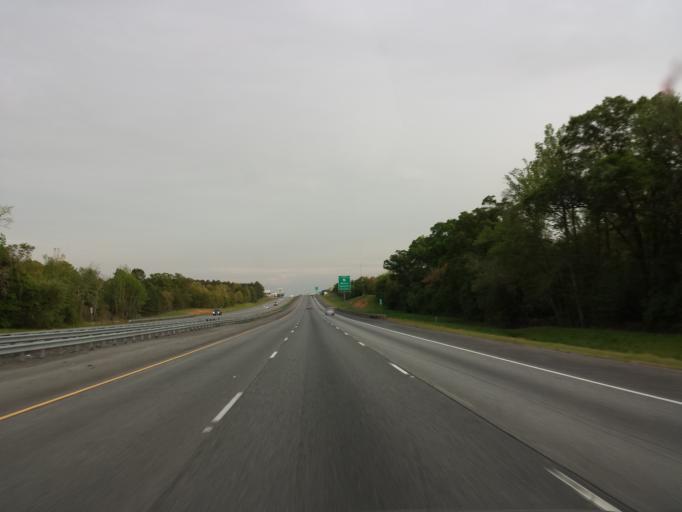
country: US
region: Georgia
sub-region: Crisp County
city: Cordele
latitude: 31.9243
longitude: -83.7450
